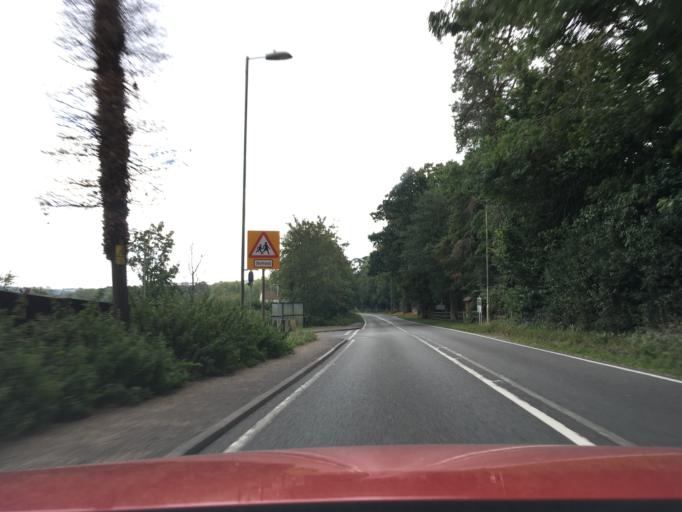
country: GB
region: England
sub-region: Hampshire
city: Kingsclere
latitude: 51.3555
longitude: -1.2567
